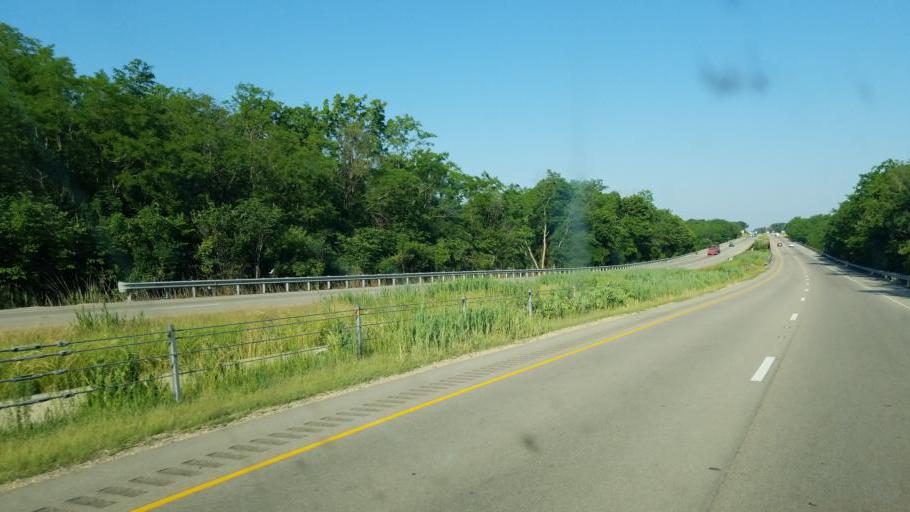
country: US
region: Illinois
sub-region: LaSalle County
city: Ottawa
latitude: 41.3775
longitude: -88.7909
